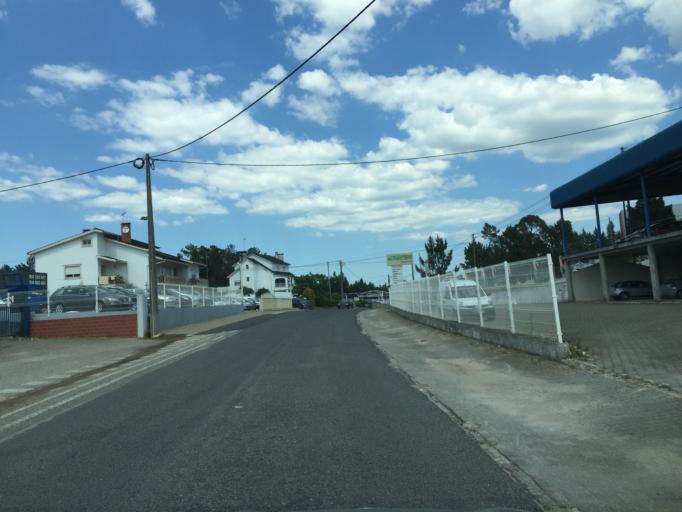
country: PT
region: Santarem
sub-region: Ourem
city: Ourem
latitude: 39.6845
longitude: -8.5618
